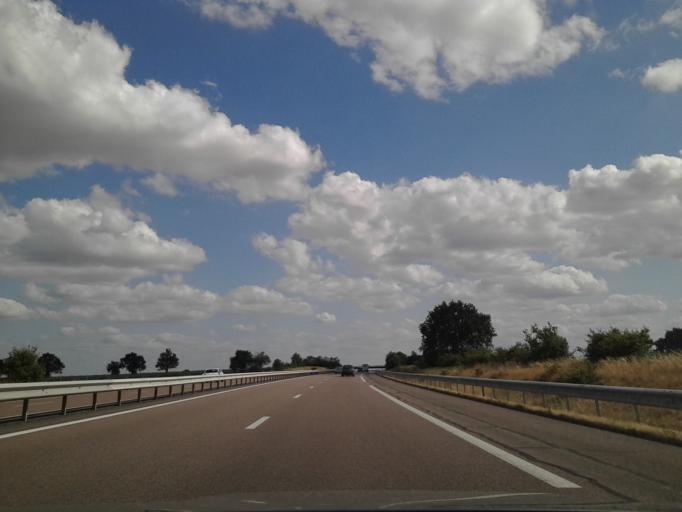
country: FR
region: Auvergne
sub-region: Departement de l'Allier
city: Estivareilles
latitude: 46.4311
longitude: 2.7001
